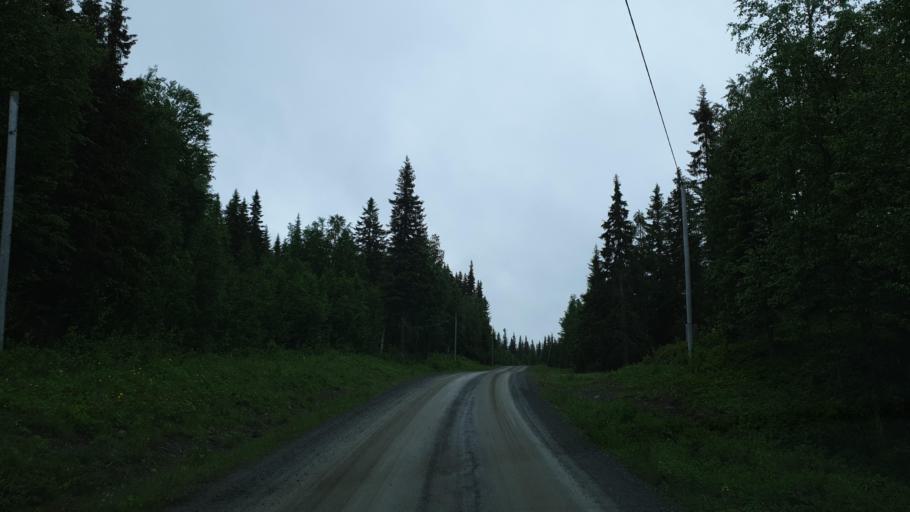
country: SE
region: Vaesterbotten
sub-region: Vilhelmina Kommun
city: Sjoberg
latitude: 65.3349
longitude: 15.8994
